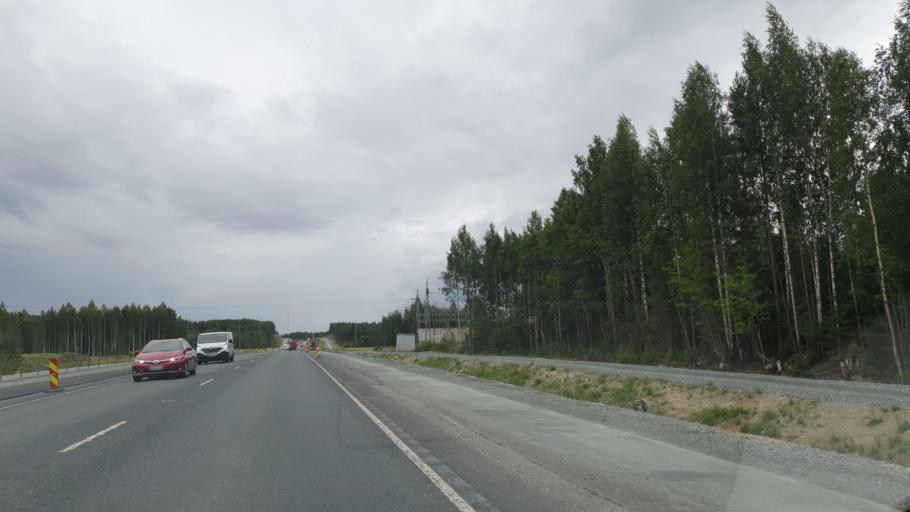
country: FI
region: Northern Savo
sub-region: Ylae-Savo
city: Lapinlahti
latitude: 63.2920
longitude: 27.4538
